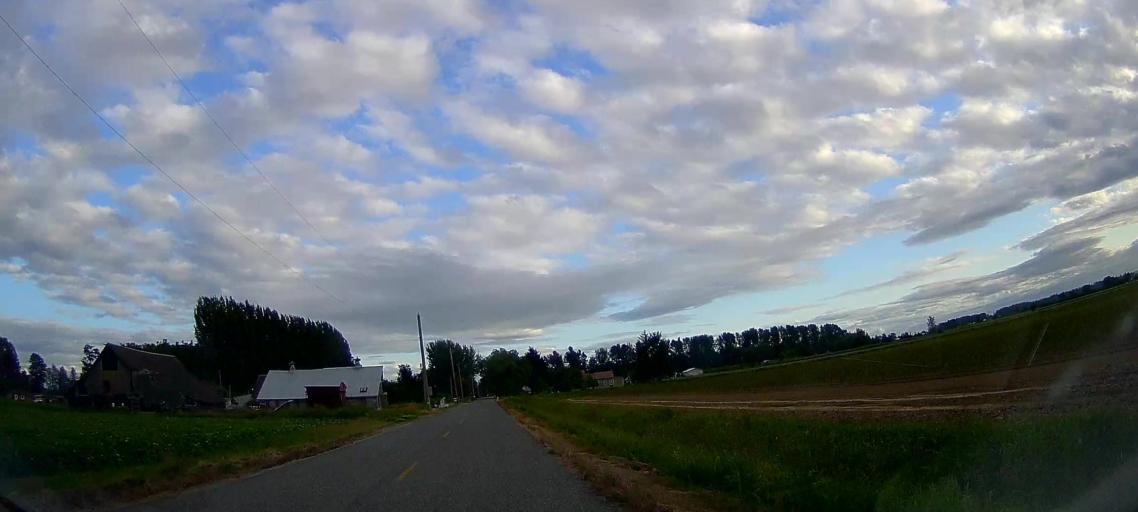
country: US
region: Washington
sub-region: Skagit County
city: Mount Vernon
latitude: 48.3893
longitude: -122.3843
